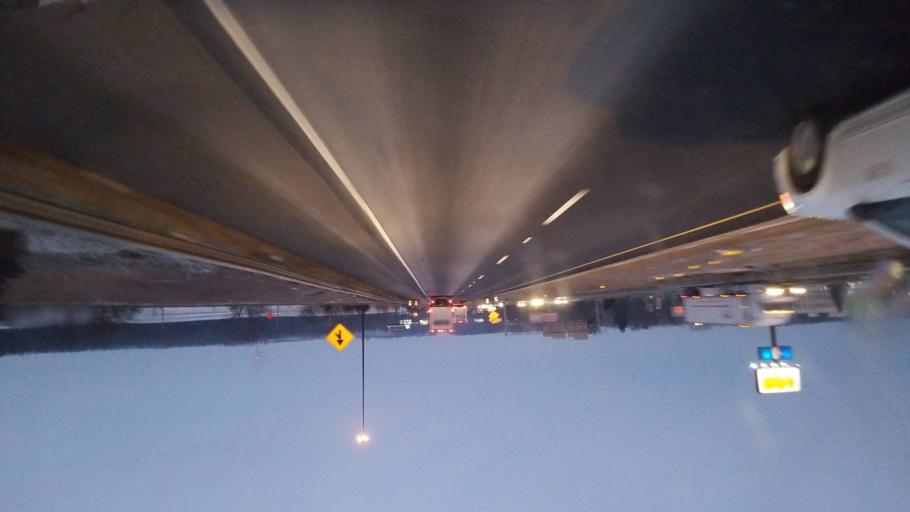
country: US
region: Ohio
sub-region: Preble County
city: New Paris
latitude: 39.8342
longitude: -84.8178
